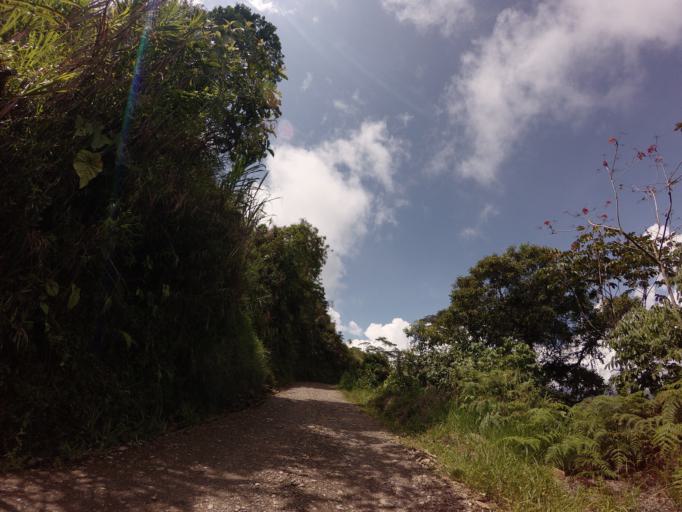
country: CO
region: Antioquia
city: Narino
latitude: 5.5125
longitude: -75.1735
